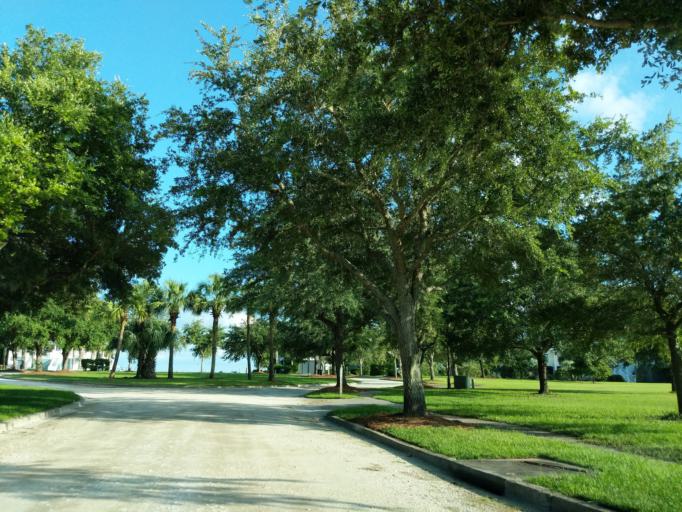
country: US
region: South Carolina
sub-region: Charleston County
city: Awendaw
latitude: 33.0803
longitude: -79.4589
